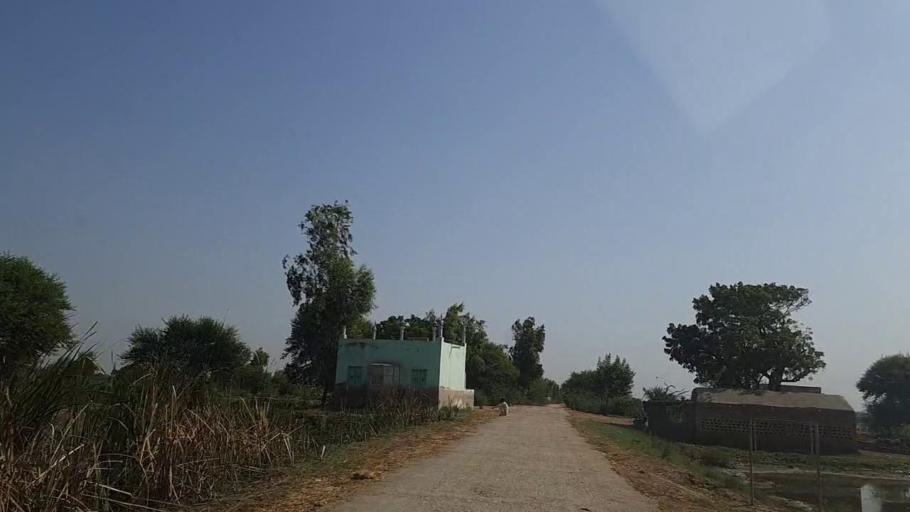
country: PK
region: Sindh
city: Daro Mehar
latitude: 24.7210
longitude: 68.0979
